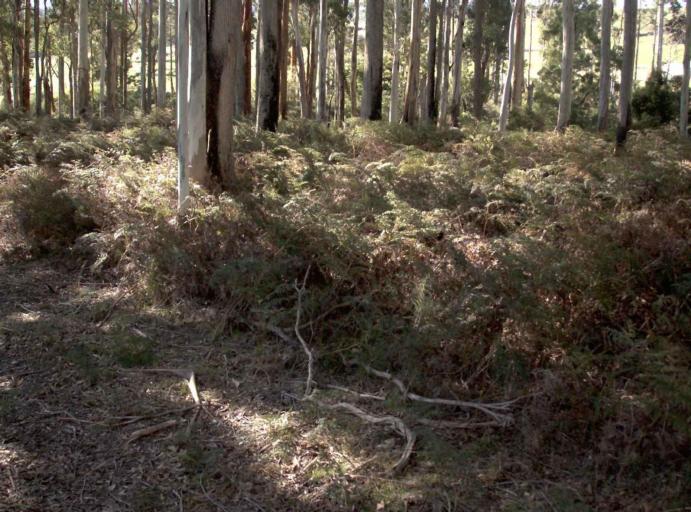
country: AU
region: Tasmania
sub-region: Launceston
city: Mayfield
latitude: -41.2507
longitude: 147.1838
